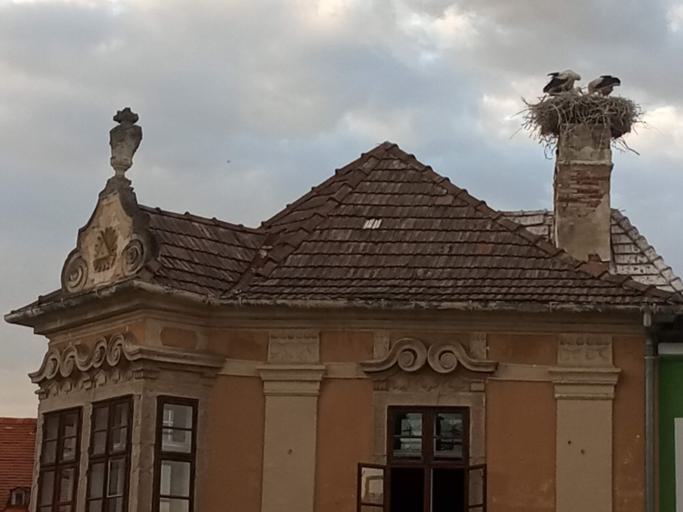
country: AT
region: Burgenland
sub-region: Rust Stadt
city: Rust
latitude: 47.8003
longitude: 16.6752
